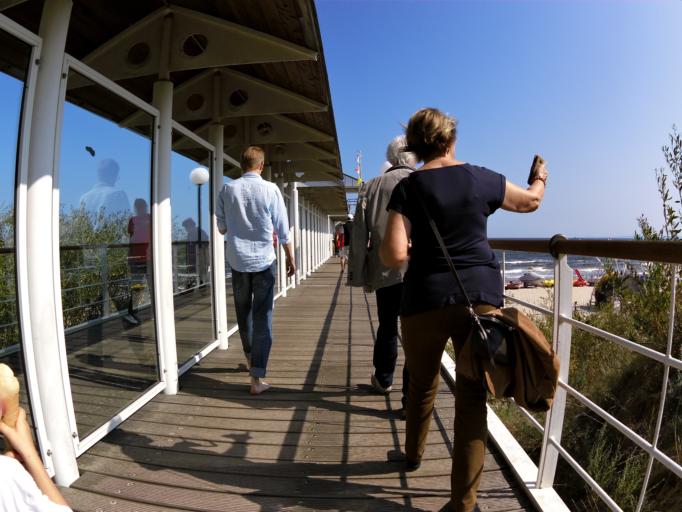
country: DE
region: Mecklenburg-Vorpommern
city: Seebad Heringsdorf
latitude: 53.9564
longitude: 14.1707
